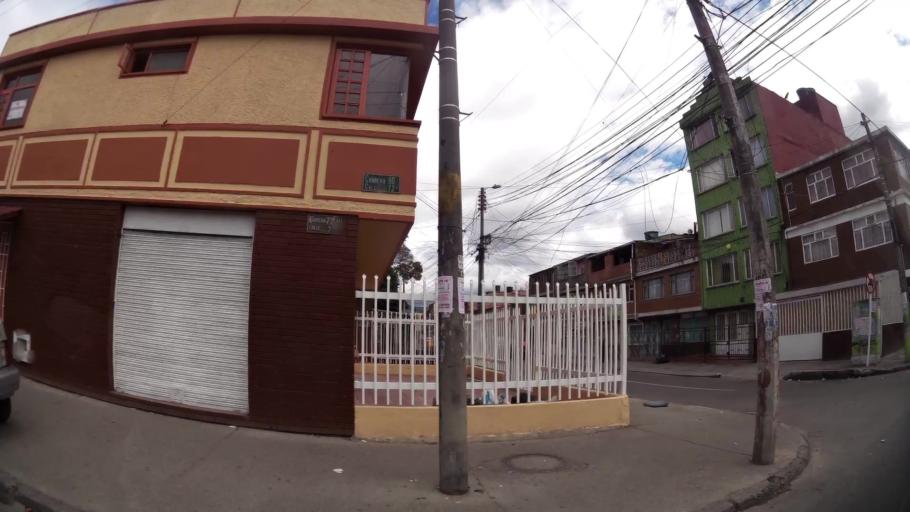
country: CO
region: Bogota D.C.
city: Barrio San Luis
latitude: 4.6930
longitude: -74.1012
